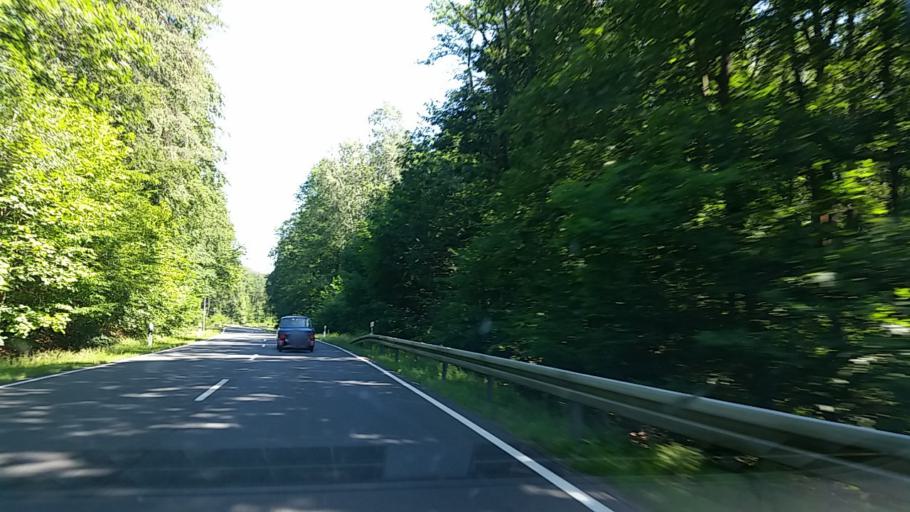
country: DE
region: Saxony
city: Bad Duben
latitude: 51.6781
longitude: 12.6072
